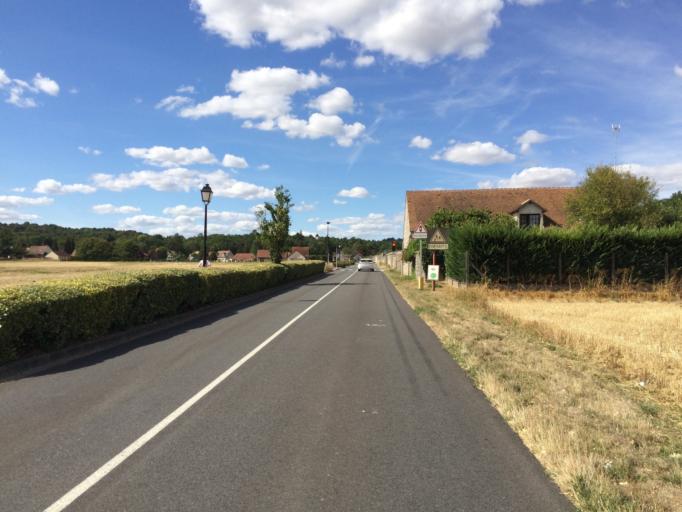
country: FR
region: Ile-de-France
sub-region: Departement de l'Essonne
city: Boutigny-sur-Essonne
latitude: 48.4350
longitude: 2.3559
